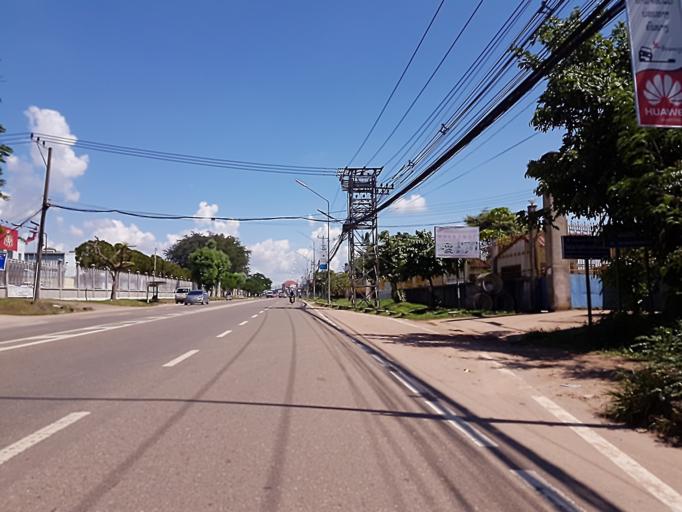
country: TH
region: Nong Khai
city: Si Chiang Mai
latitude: 17.9023
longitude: 102.6309
